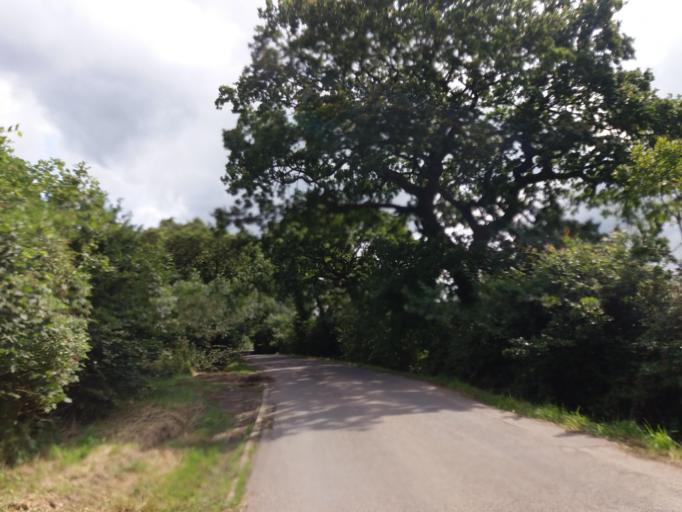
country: GB
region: England
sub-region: Lancashire
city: Euxton
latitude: 53.6681
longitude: -2.6673
